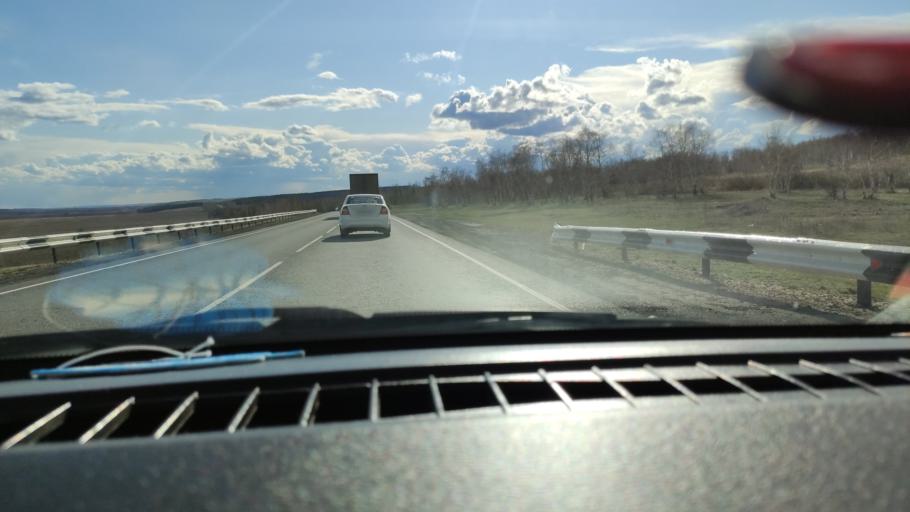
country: RU
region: Saratov
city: Sennoy
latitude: 52.1330
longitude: 46.8651
